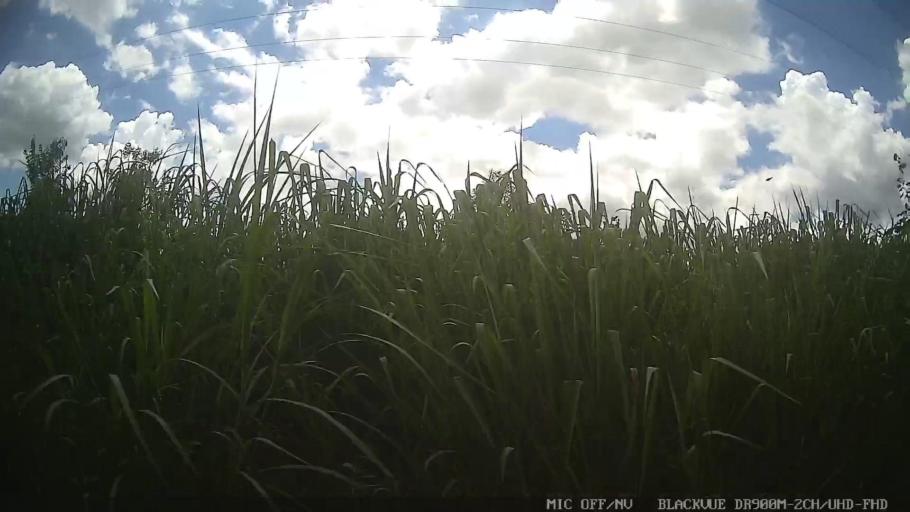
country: BR
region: Sao Paulo
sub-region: Bom Jesus Dos Perdoes
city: Bom Jesus dos Perdoes
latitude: -23.0366
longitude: -46.4825
